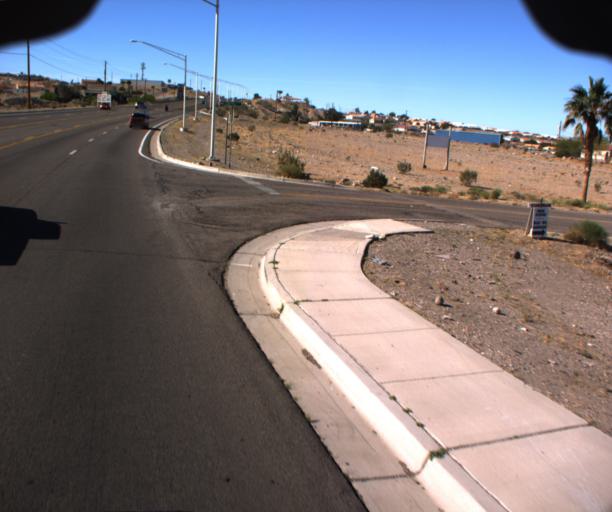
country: US
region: Arizona
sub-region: Mohave County
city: Bullhead City
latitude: 35.0481
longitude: -114.5890
